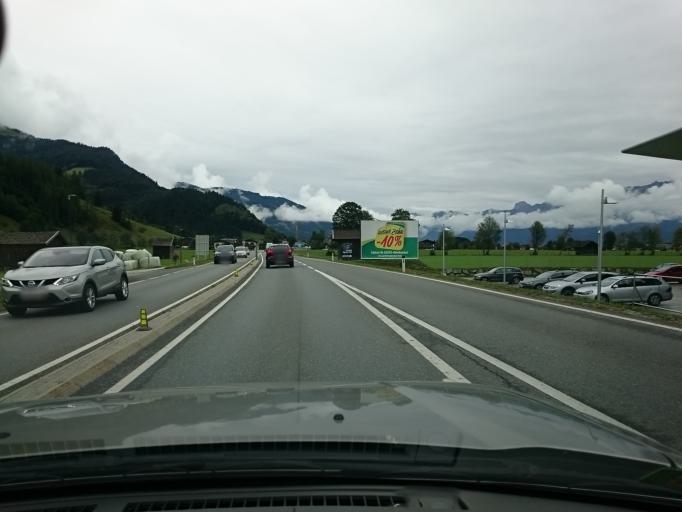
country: AT
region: Salzburg
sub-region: Politischer Bezirk Zell am See
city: Maishofen
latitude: 47.3518
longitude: 12.8002
